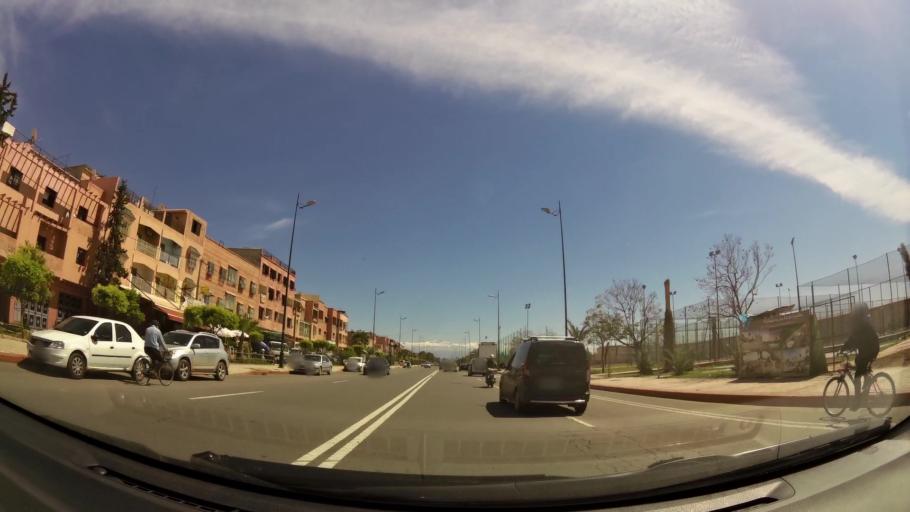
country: MA
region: Marrakech-Tensift-Al Haouz
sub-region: Marrakech
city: Marrakesh
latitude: 31.6078
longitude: -7.9731
